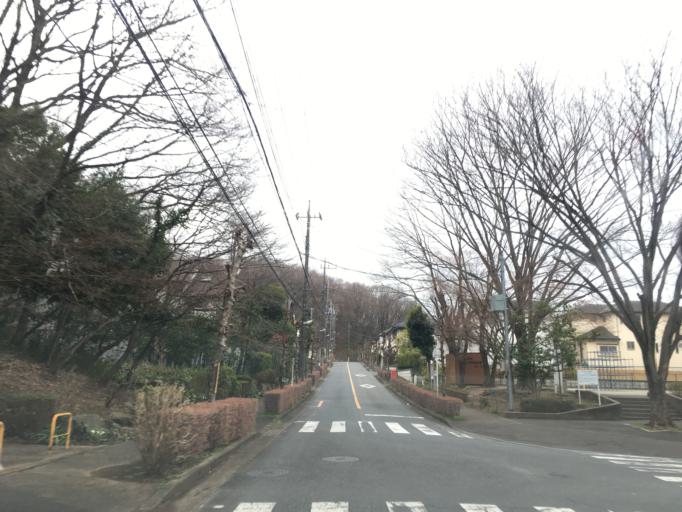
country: JP
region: Tokyo
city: Higashimurayama-shi
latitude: 35.7746
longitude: 139.4602
